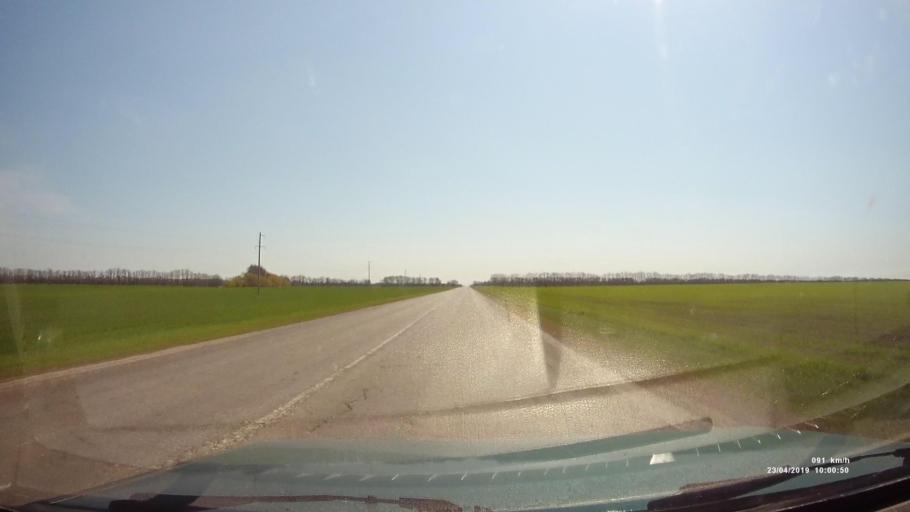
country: RU
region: Rostov
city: Sovetskoye
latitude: 46.7685
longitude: 42.1389
